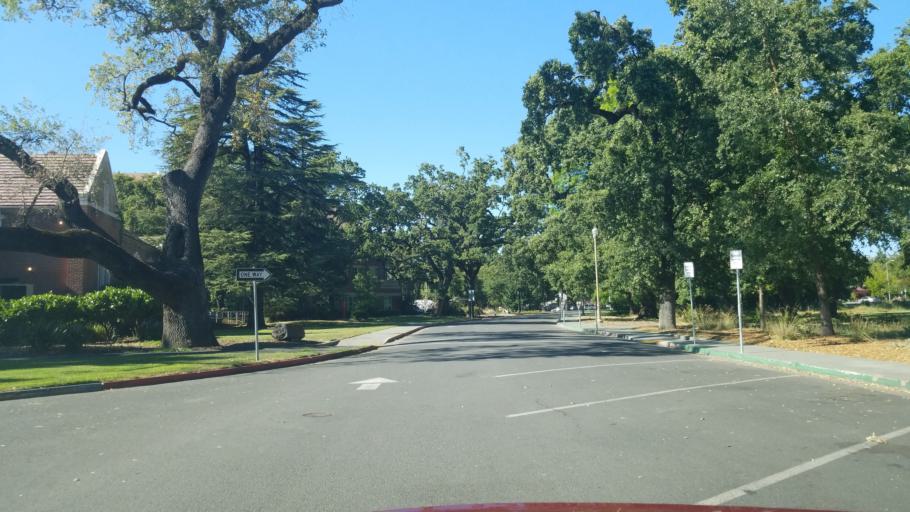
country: US
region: California
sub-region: Sonoma County
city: Santa Rosa
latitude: 38.4561
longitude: -122.7186
